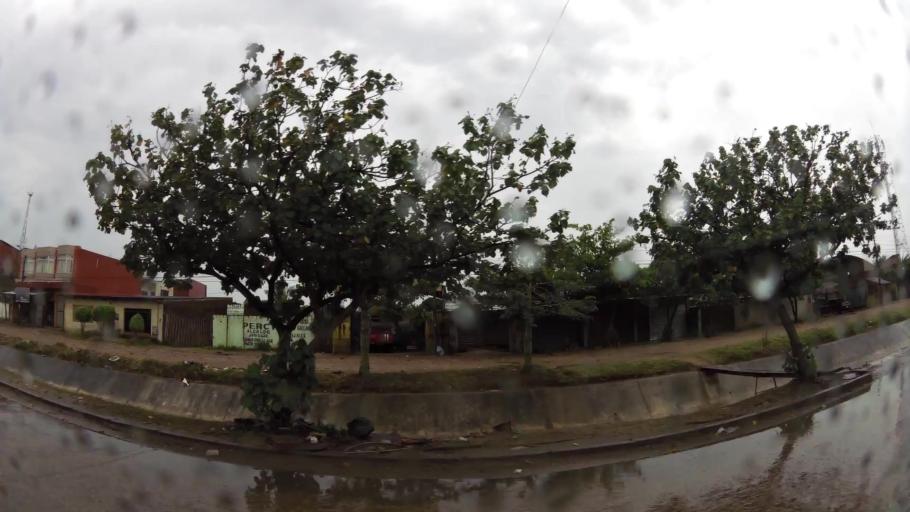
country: BO
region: Santa Cruz
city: Santa Cruz de la Sierra
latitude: -17.8048
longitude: -63.1280
